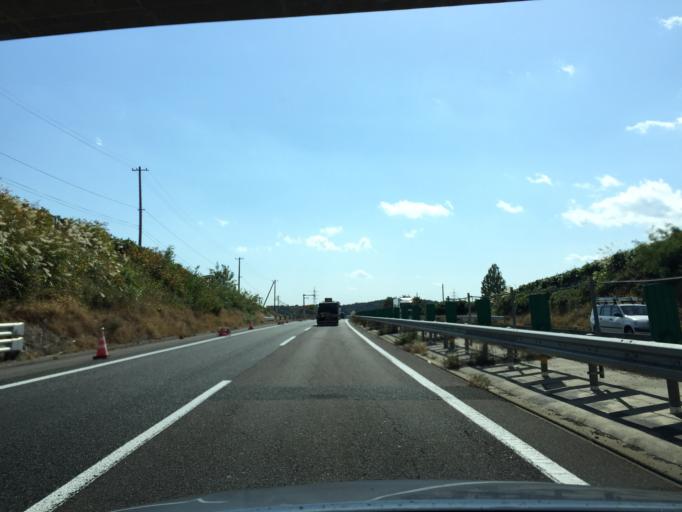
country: JP
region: Fukushima
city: Sukagawa
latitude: 37.3356
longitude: 140.3368
